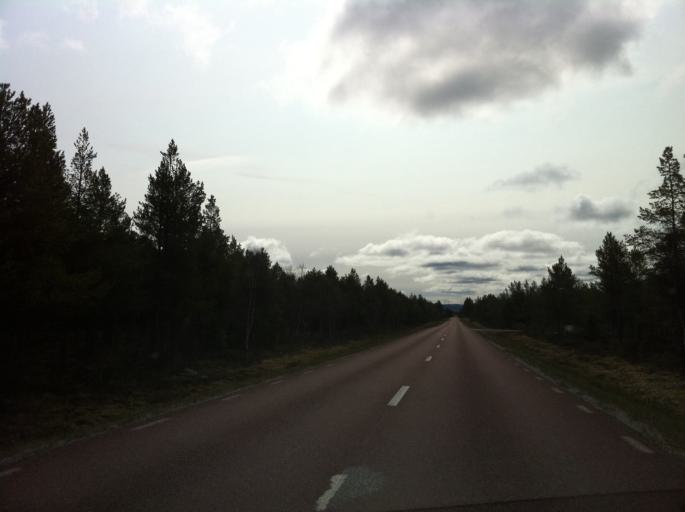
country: NO
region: Hedmark
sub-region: Engerdal
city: Engerdal
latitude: 62.4850
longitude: 12.6548
